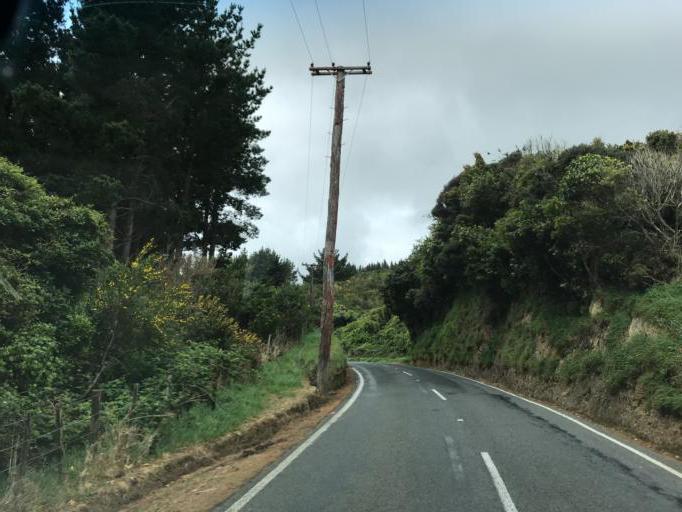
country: NZ
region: Wellington
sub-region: Wellington City
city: Kelburn
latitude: -41.2129
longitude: 174.7923
